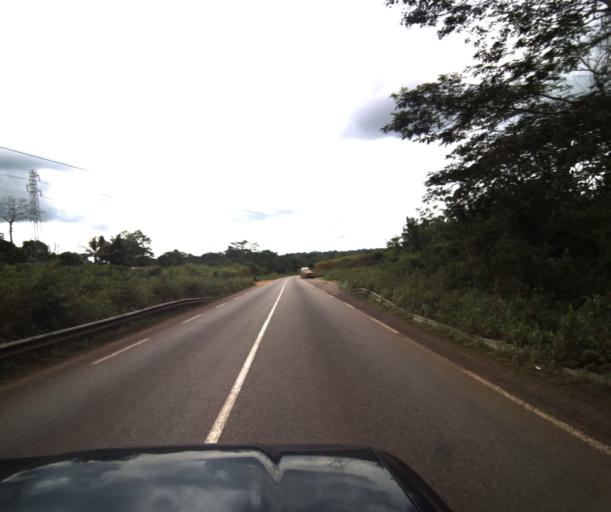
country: CM
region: Littoral
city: Edea
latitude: 3.8162
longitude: 10.3596
